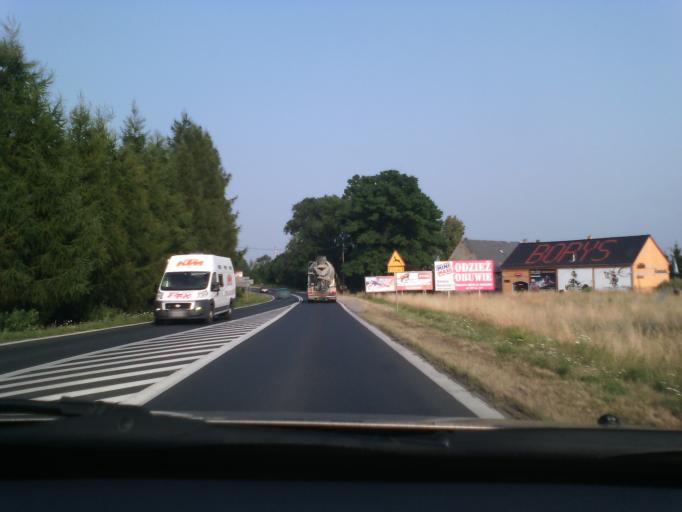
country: PL
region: Lower Silesian Voivodeship
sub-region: Jelenia Gora
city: Cieplice Slaskie Zdroj
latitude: 50.8923
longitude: 15.6835
